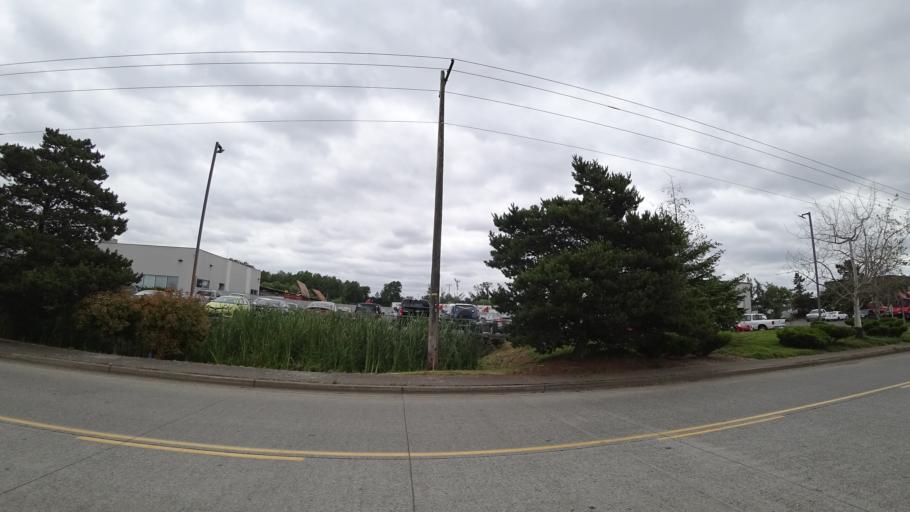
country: US
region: Washington
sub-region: Clark County
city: Vancouver
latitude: 45.5861
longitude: -122.6520
